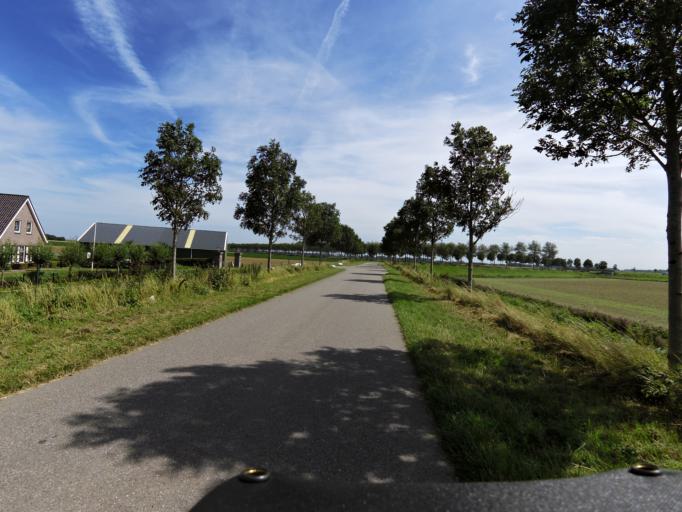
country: NL
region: South Holland
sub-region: Gemeente Goeree-Overflakkee
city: Dirksland
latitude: 51.7846
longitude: 4.0798
